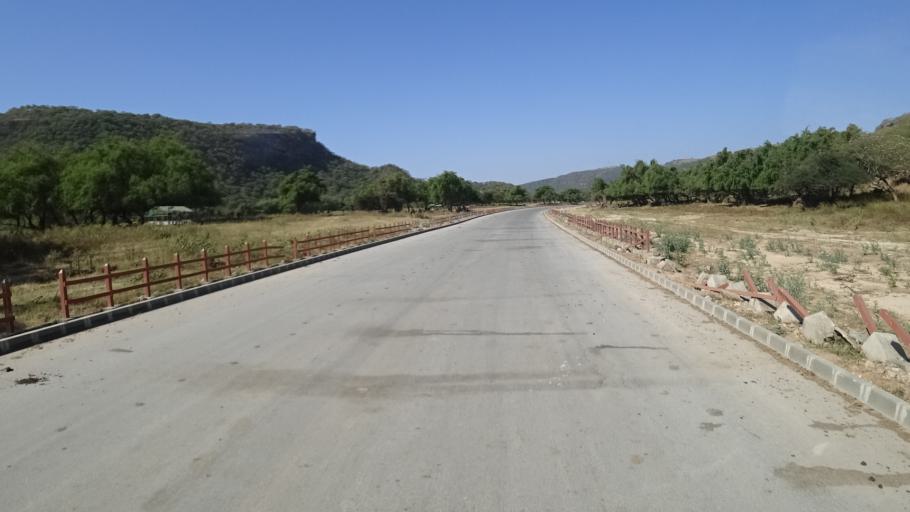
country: OM
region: Zufar
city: Salalah
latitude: 17.0910
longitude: 54.4451
